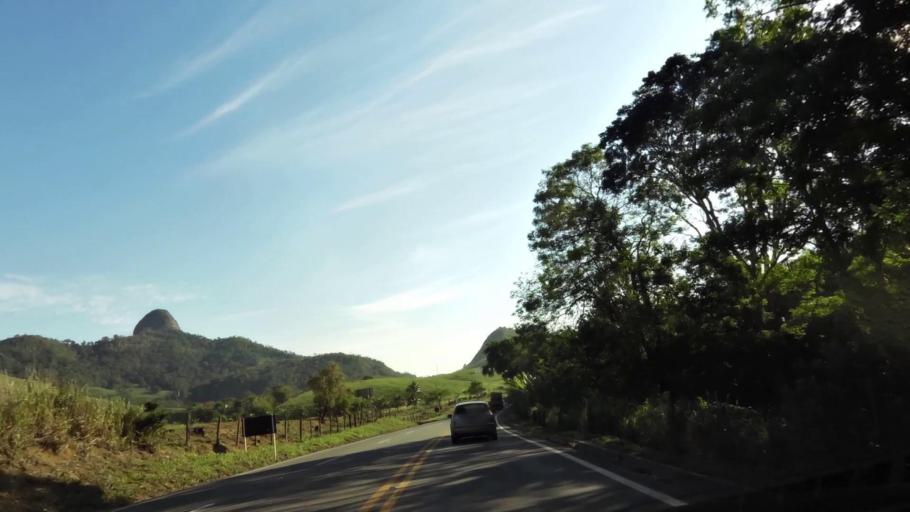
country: BR
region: Espirito Santo
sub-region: Guarapari
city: Guarapari
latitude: -20.5281
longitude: -40.4822
